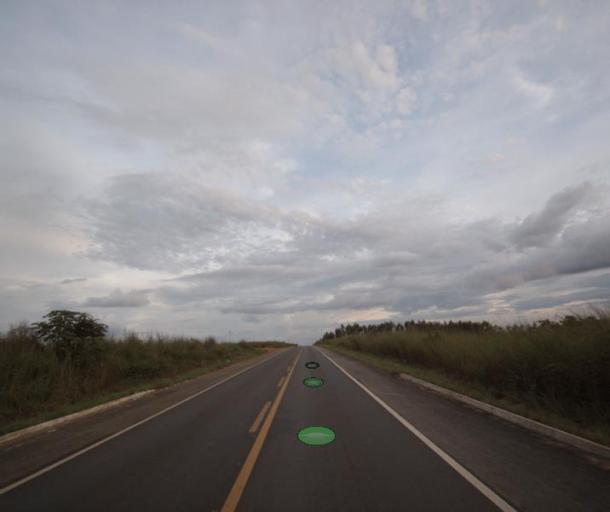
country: BR
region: Goias
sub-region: Barro Alto
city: Barro Alto
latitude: -15.2017
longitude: -48.7017
